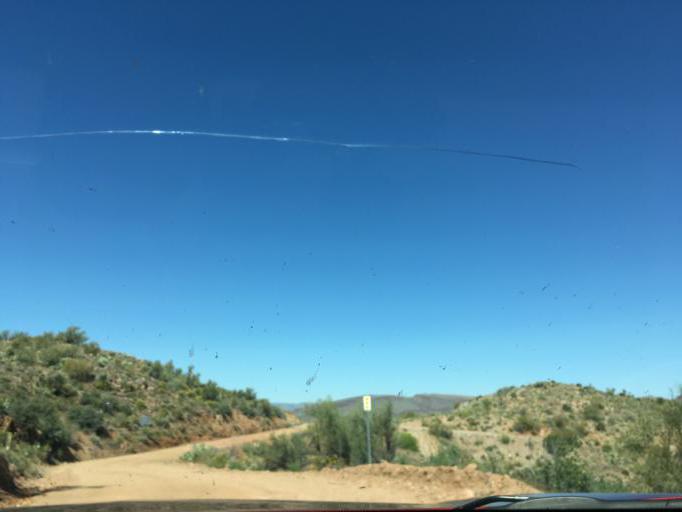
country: US
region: Arizona
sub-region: Yavapai County
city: Bagdad
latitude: 34.6098
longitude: -113.4015
